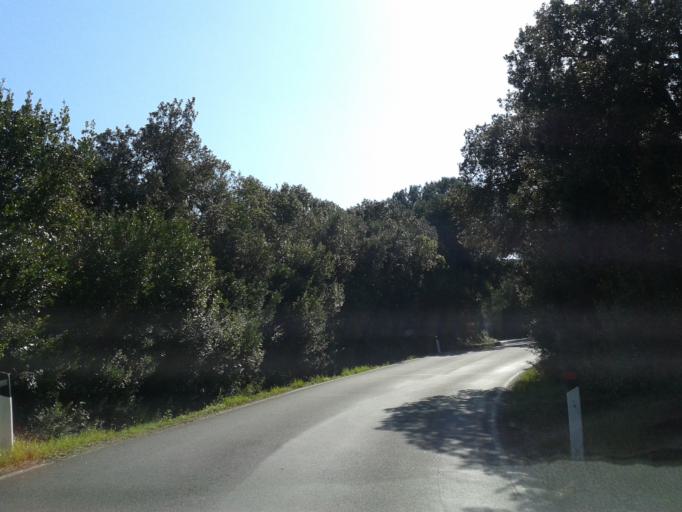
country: IT
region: Tuscany
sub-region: Provincia di Livorno
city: Quercianella
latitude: 43.4527
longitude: 10.3910
